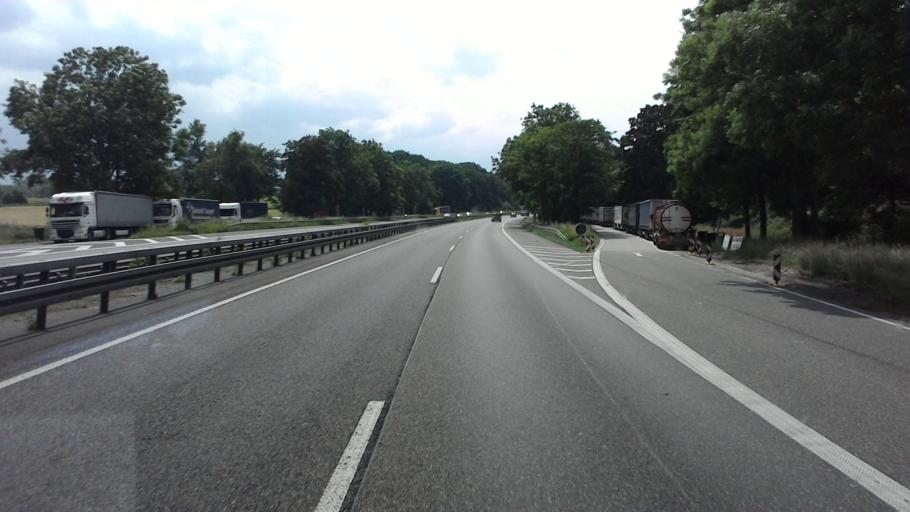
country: DE
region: North Rhine-Westphalia
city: Stolberg
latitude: 50.7692
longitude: 6.1740
